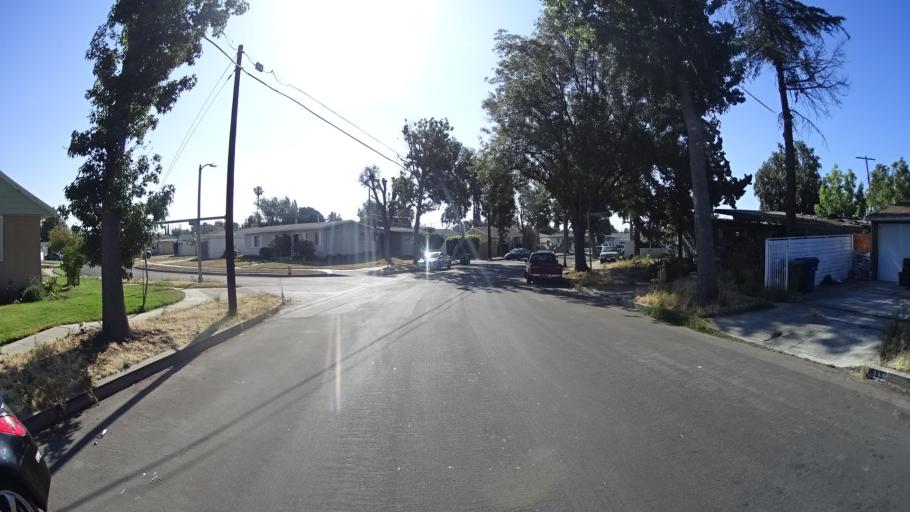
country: US
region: California
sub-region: Los Angeles County
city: Van Nuys
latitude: 34.2258
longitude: -118.4294
